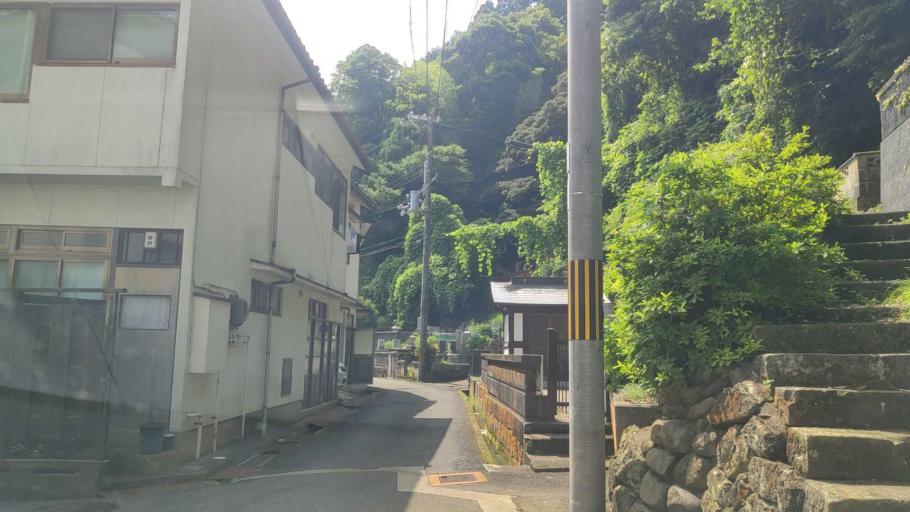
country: JP
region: Hyogo
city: Toyooka
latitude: 35.6247
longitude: 134.8107
